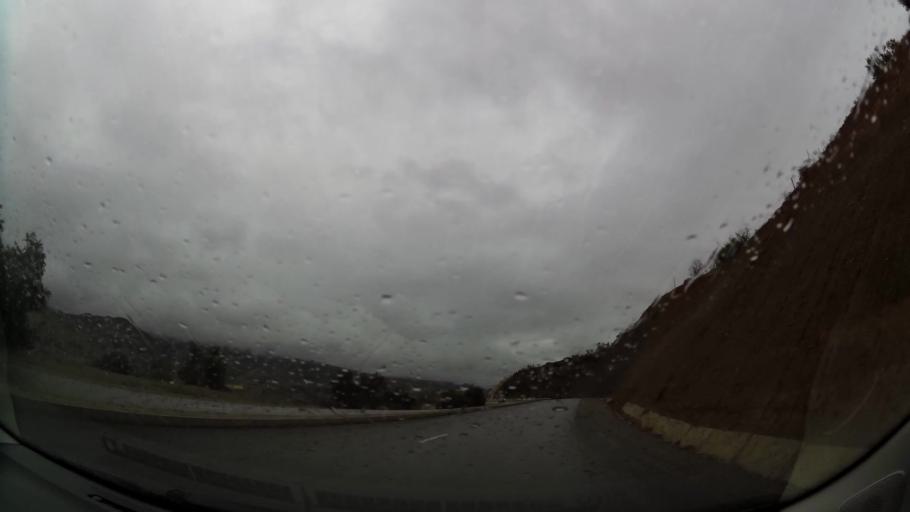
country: MA
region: Taza-Al Hoceima-Taounate
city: Imzourene
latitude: 34.9943
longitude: -3.8114
